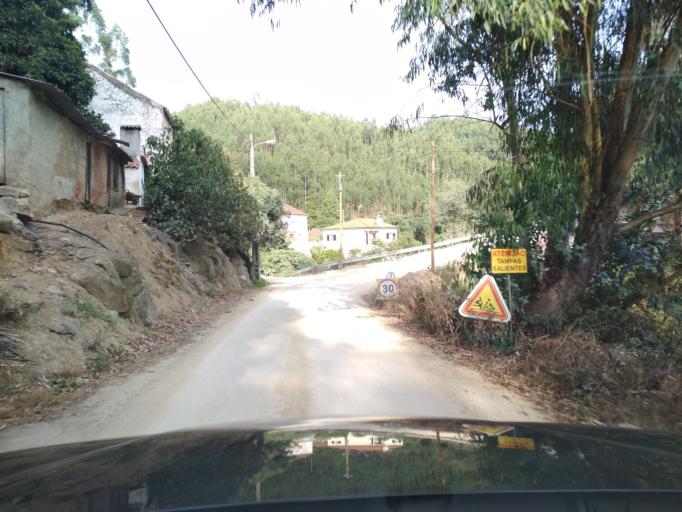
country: PT
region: Coimbra
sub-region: Coimbra
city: Coimbra
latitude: 40.2512
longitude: -8.3815
